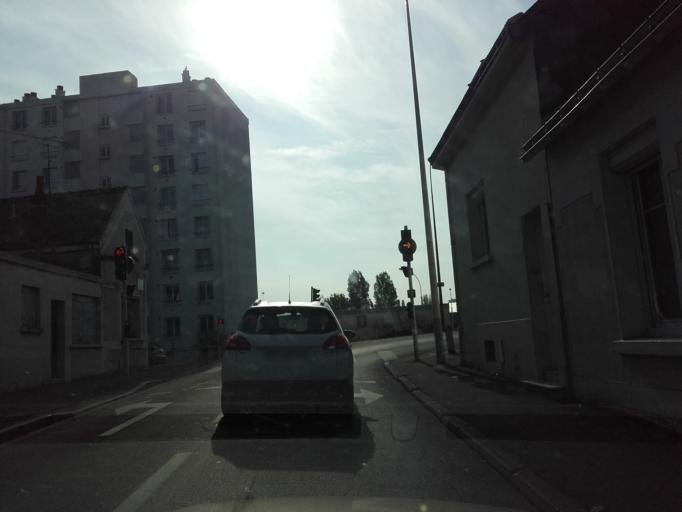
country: FR
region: Centre
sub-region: Departement d'Indre-et-Loire
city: Tours
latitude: 47.3763
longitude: 0.6789
